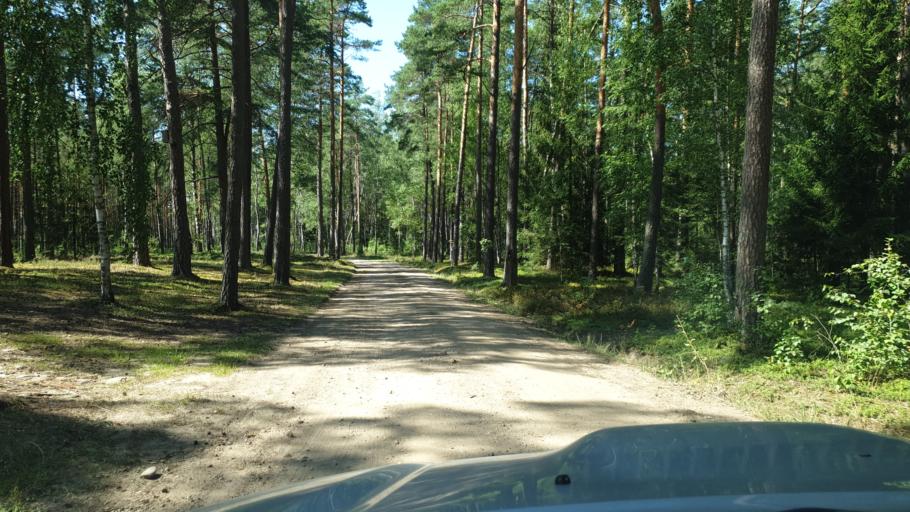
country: LT
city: Sirvintos
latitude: 54.9074
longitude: 24.9544
